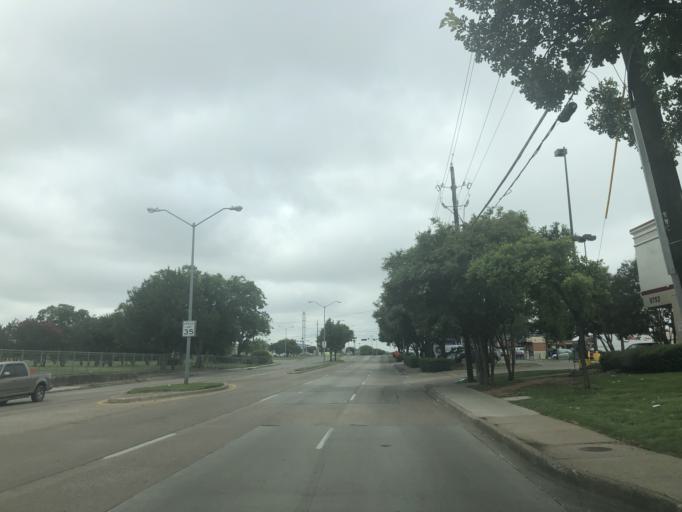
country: US
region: Texas
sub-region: Dallas County
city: Farmers Branch
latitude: 32.8684
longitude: -96.8649
